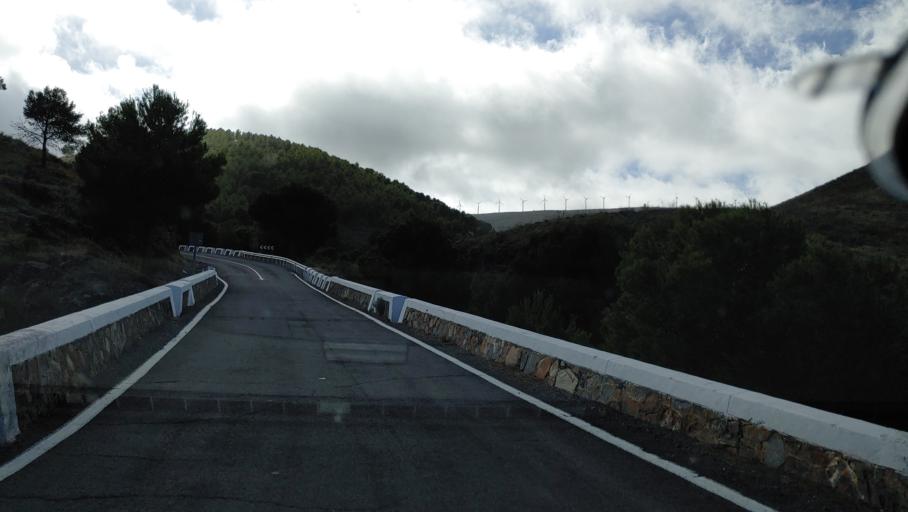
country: ES
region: Andalusia
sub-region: Provincia de Almeria
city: Enix
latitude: 36.9151
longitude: -2.6024
